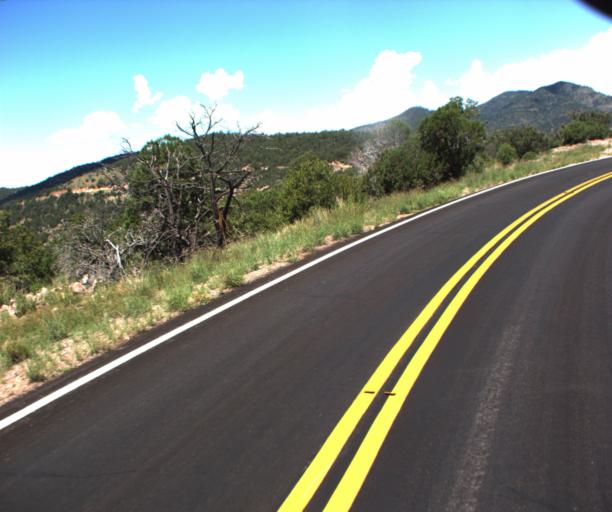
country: US
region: Arizona
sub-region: Greenlee County
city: Morenci
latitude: 33.3989
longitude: -109.3376
